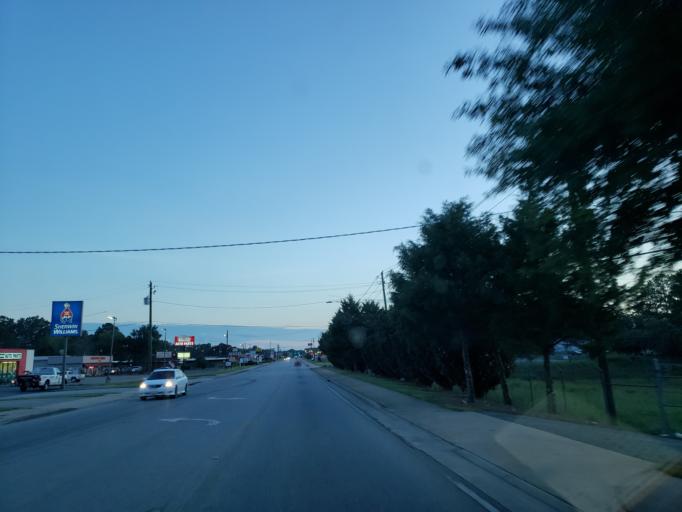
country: US
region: Georgia
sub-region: Polk County
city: Cedartown
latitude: 34.0291
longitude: -85.2479
